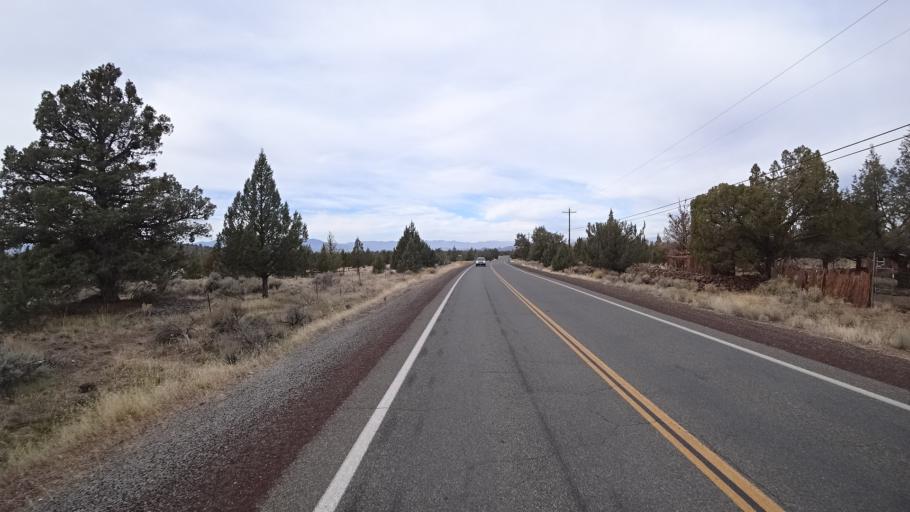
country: US
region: California
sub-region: Siskiyou County
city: Weed
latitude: 41.6050
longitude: -122.3587
